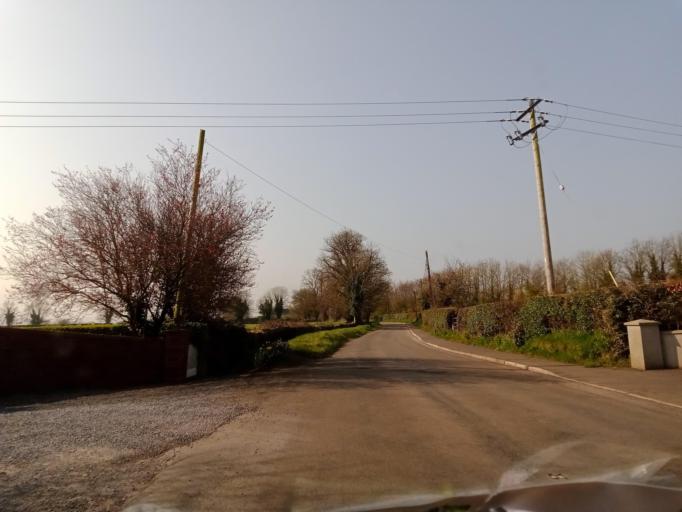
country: IE
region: Leinster
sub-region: Kilkenny
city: Callan
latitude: 52.5376
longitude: -7.3961
